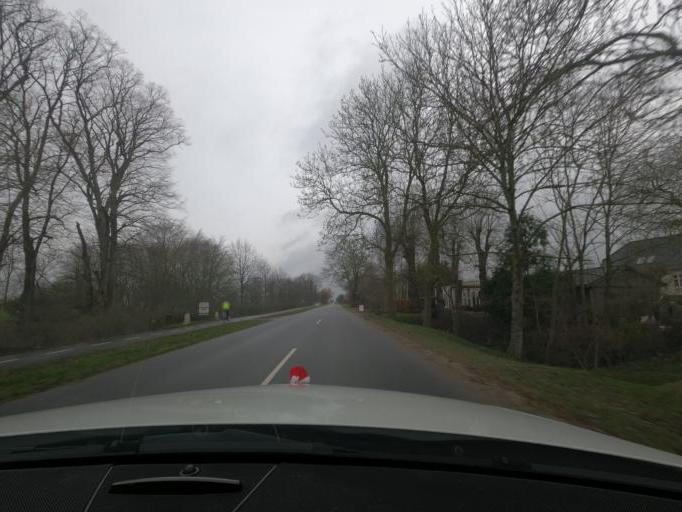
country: DK
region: South Denmark
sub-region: Haderslev Kommune
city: Starup
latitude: 55.1946
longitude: 9.5626
